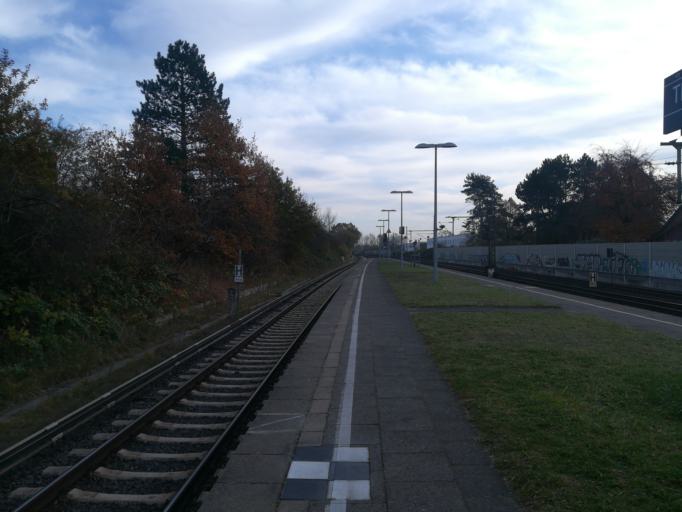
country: DE
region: Schleswig-Holstein
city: Rellingen
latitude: 53.6436
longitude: 9.8150
